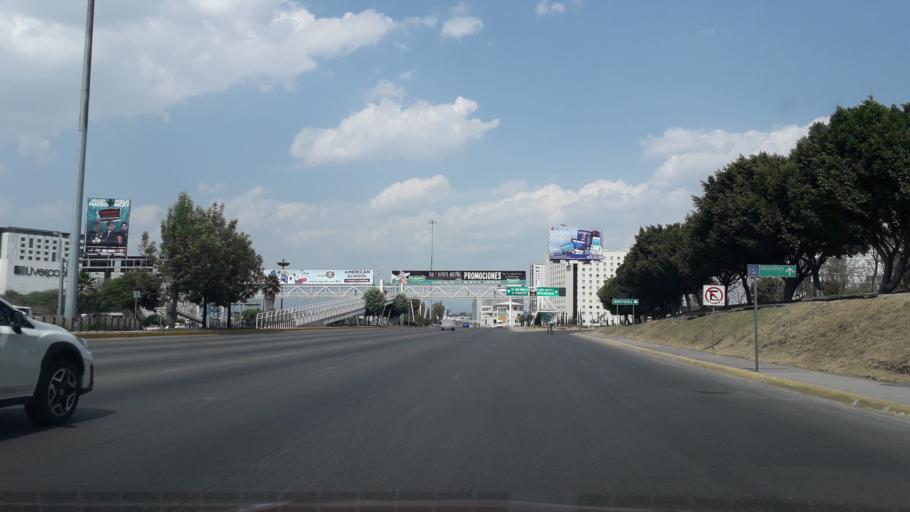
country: MX
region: Puebla
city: Puebla
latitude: 19.0288
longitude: -98.2321
